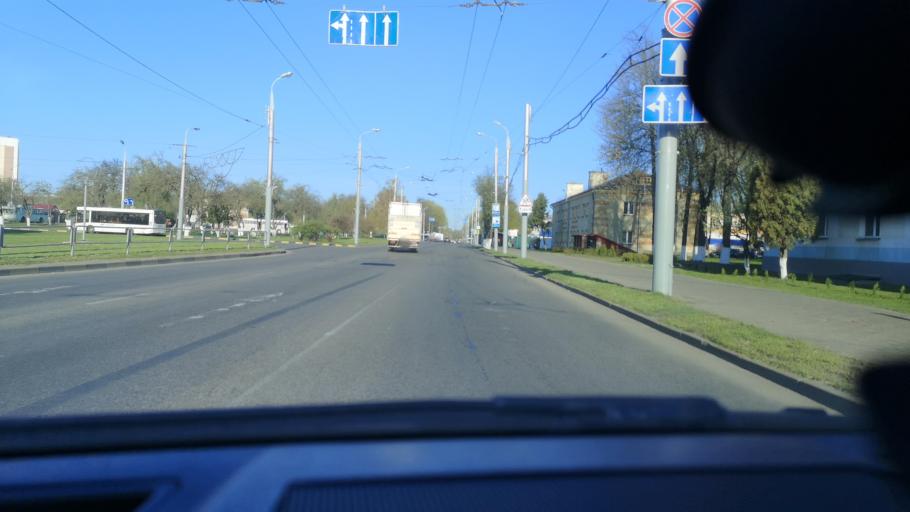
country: BY
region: Gomel
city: Gomel
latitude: 52.4191
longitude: 30.9722
